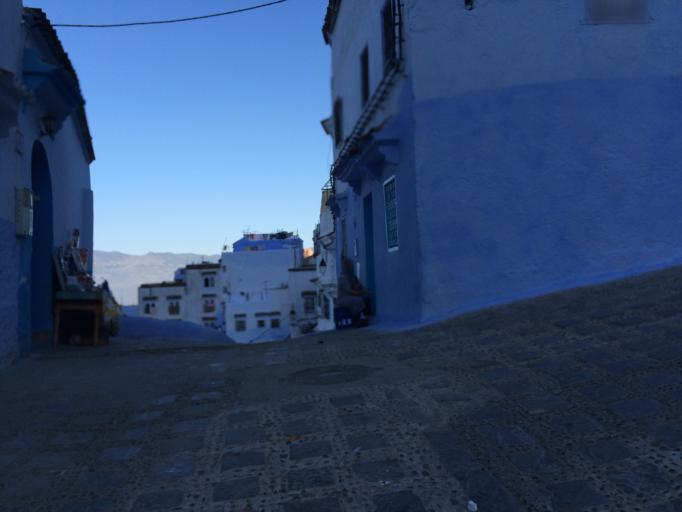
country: MA
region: Tanger-Tetouan
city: Chefchaouene
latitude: 35.1711
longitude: -5.2605
